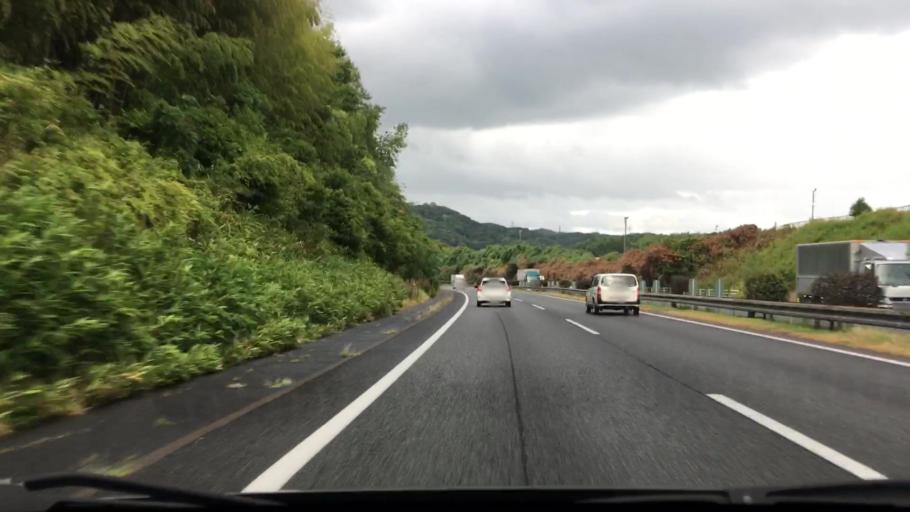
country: JP
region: Fukuoka
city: Miyata
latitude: 33.7442
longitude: 130.6229
